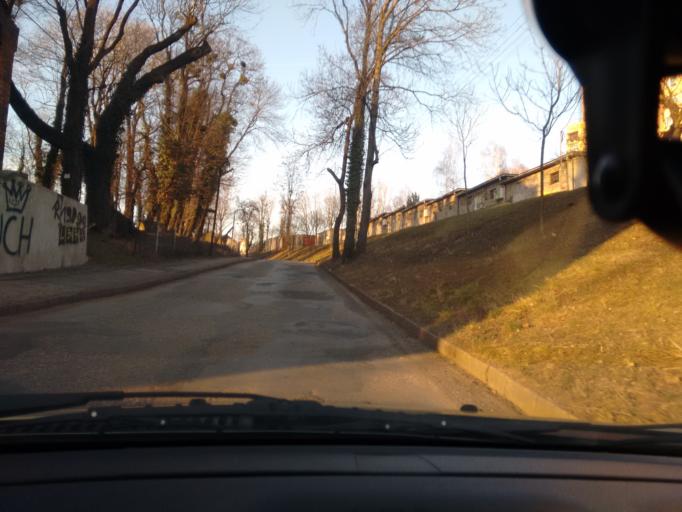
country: PL
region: Silesian Voivodeship
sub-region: Powiat cieszynski
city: Cieszyn
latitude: 49.7559
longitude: 18.6292
